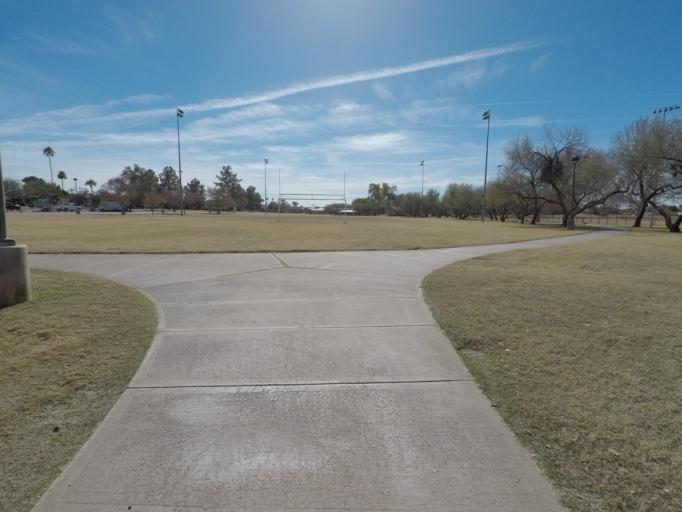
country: US
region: Arizona
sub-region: Maricopa County
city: Scottsdale
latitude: 33.4718
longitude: -111.9151
